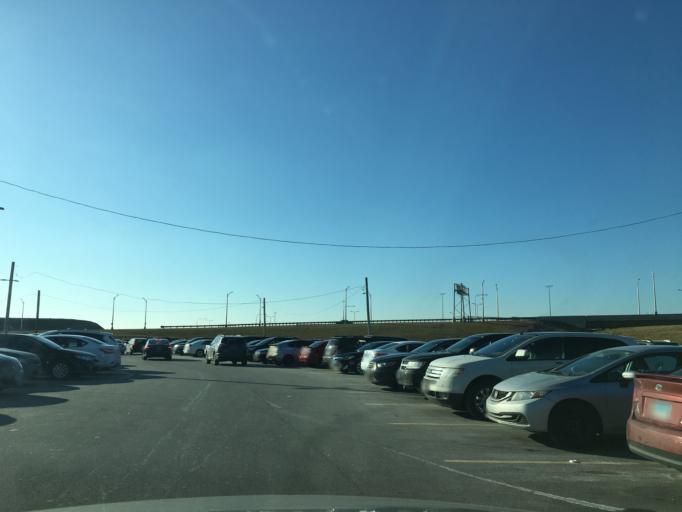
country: US
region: Illinois
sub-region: Cook County
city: Rosemont
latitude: 41.9780
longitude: -87.8771
